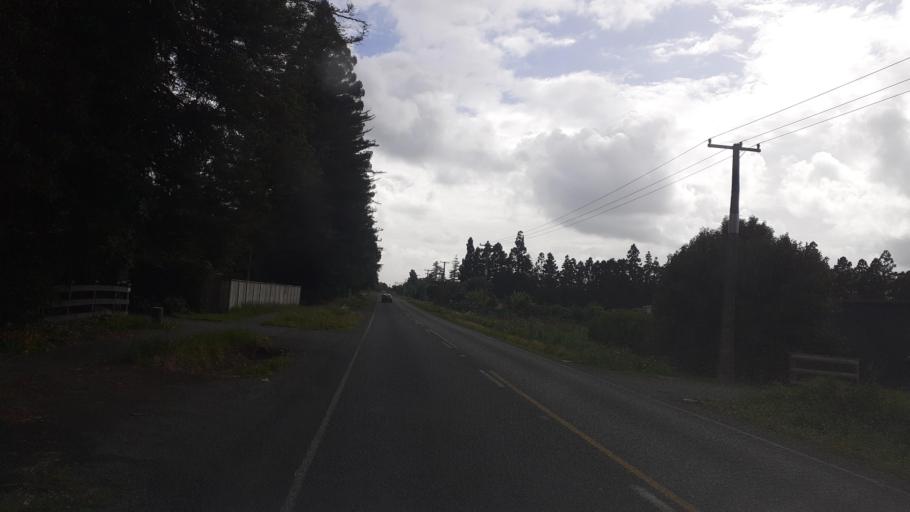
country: NZ
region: Northland
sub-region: Far North District
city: Kerikeri
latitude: -35.2260
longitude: 173.9701
